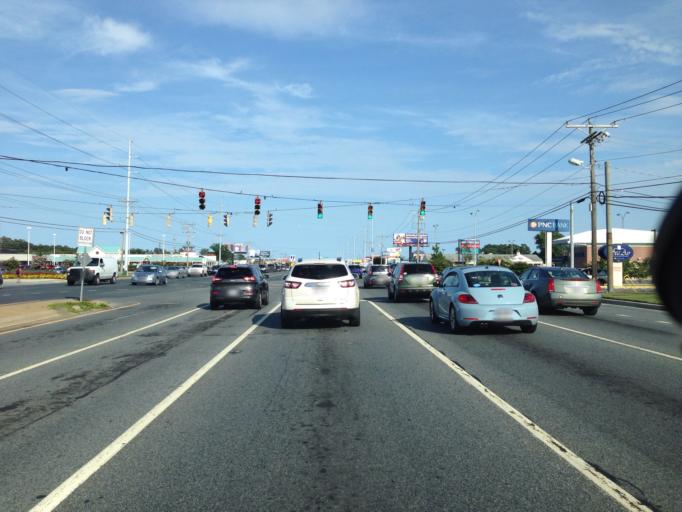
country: US
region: Delaware
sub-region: Sussex County
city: Rehoboth Beach
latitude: 38.7181
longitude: -75.1138
